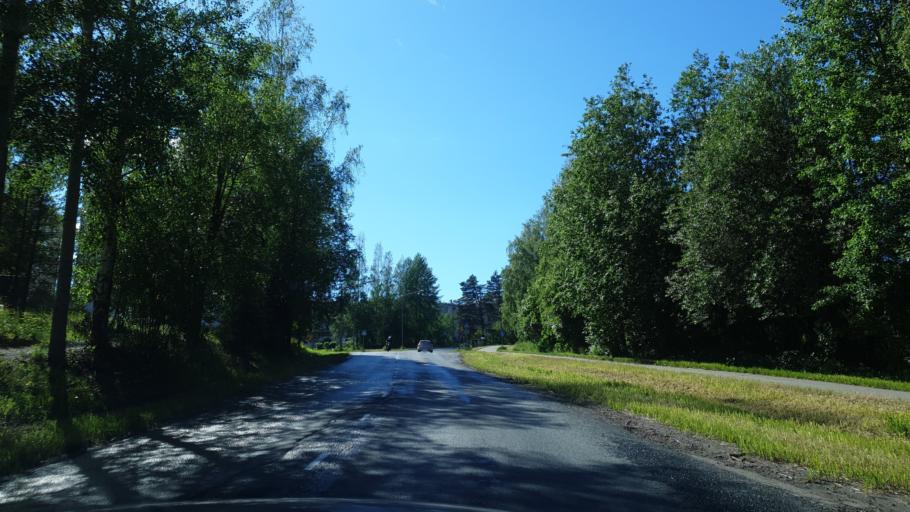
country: FI
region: Northern Savo
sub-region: Kuopio
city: Kuopio
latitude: 62.9059
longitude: 27.6513
